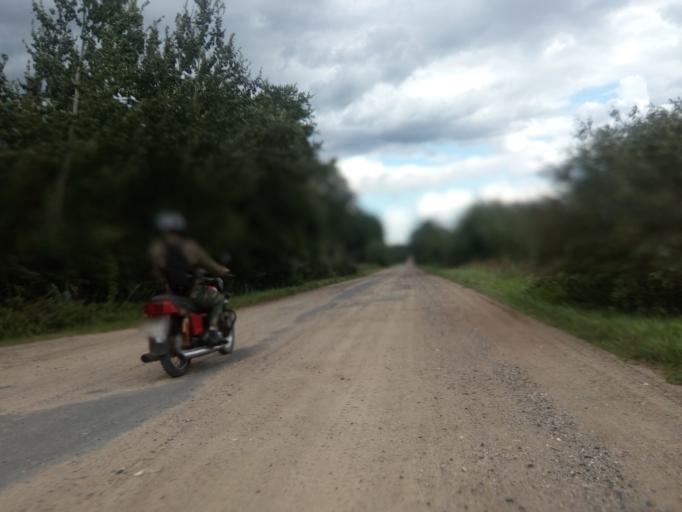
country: BY
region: Vitebsk
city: Dzisna
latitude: 55.7086
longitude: 28.3092
